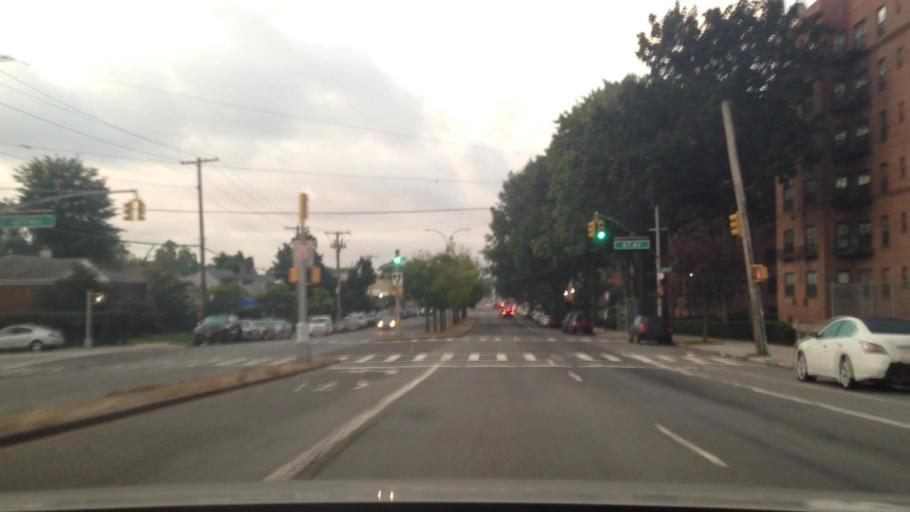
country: US
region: New York
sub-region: Queens County
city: Jamaica
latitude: 40.7353
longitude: -73.8049
